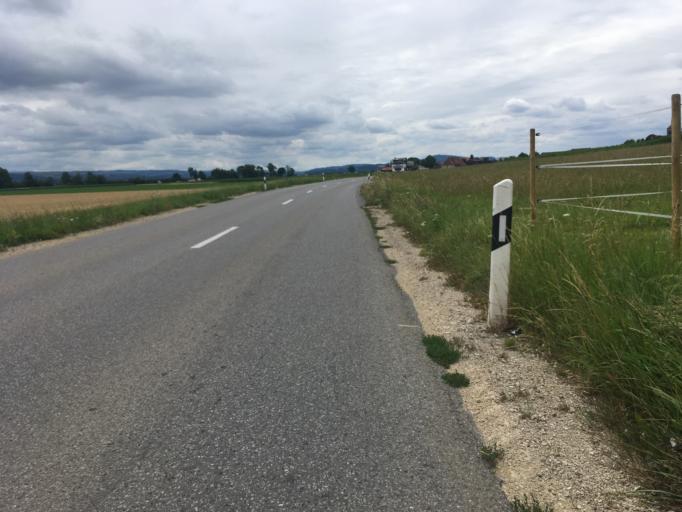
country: CH
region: Vaud
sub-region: Broye-Vully District
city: Payerne
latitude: 46.8738
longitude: 6.9537
